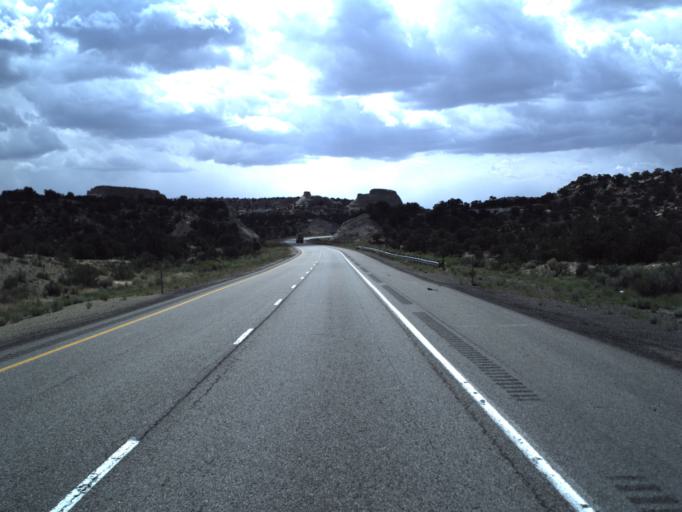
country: US
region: Utah
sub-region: Emery County
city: Ferron
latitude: 38.8602
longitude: -110.8671
